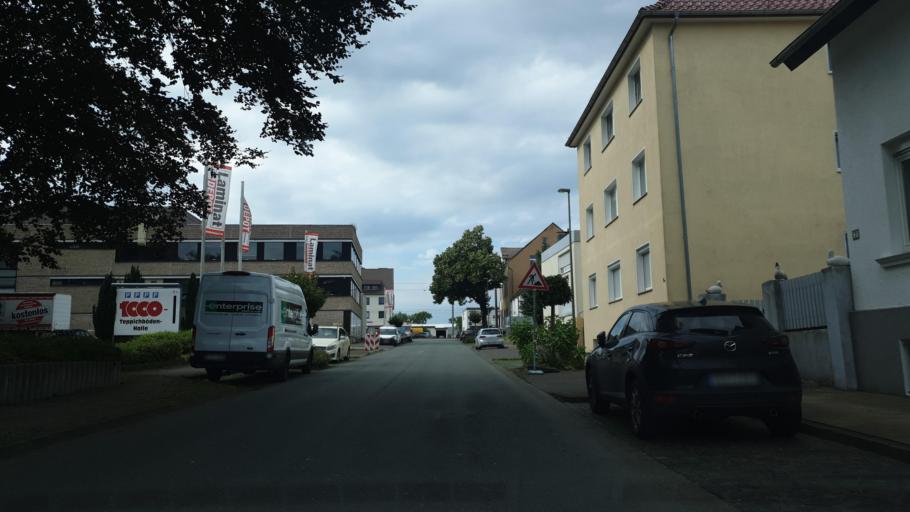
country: DE
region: North Rhine-Westphalia
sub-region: Regierungsbezirk Detmold
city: Bielefeld
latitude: 52.0345
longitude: 8.5539
